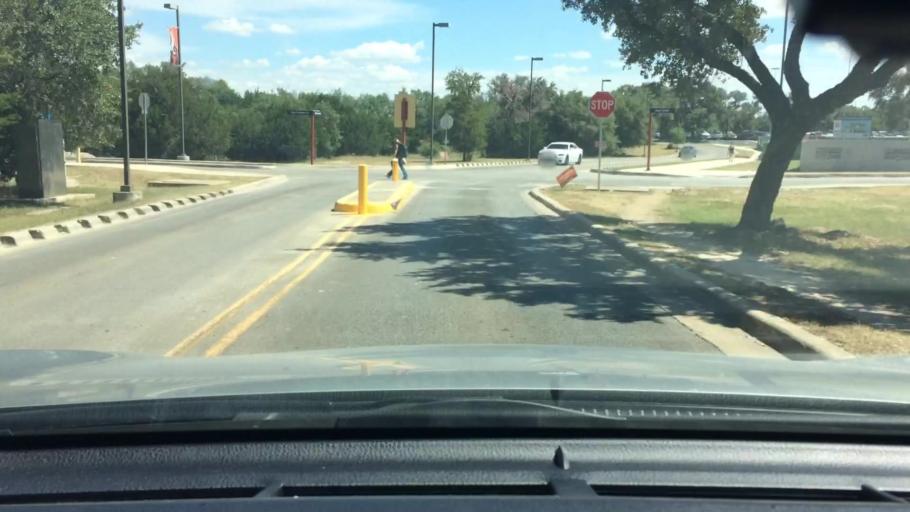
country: US
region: Texas
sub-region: Bexar County
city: Shavano Park
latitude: 29.5833
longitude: -98.6151
